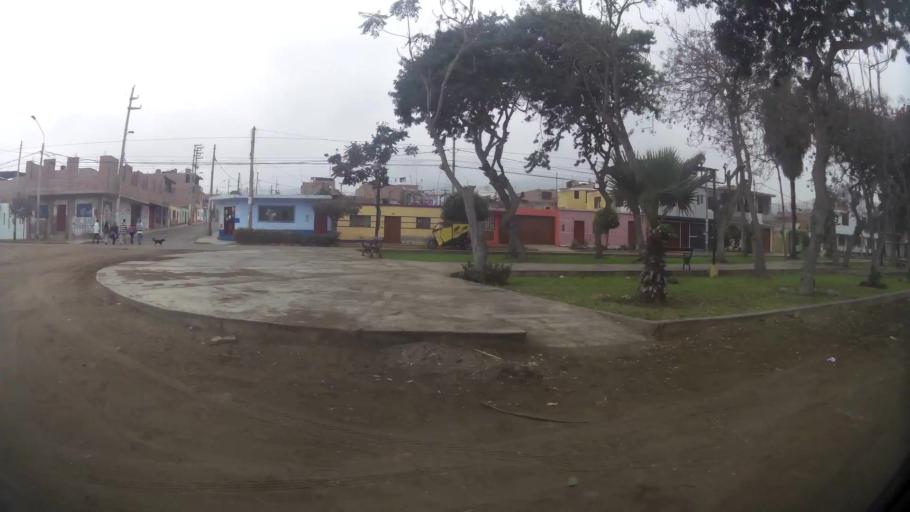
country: PE
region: Lima
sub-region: Provincia de Huaral
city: Chancay
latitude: -11.5906
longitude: -77.2607
